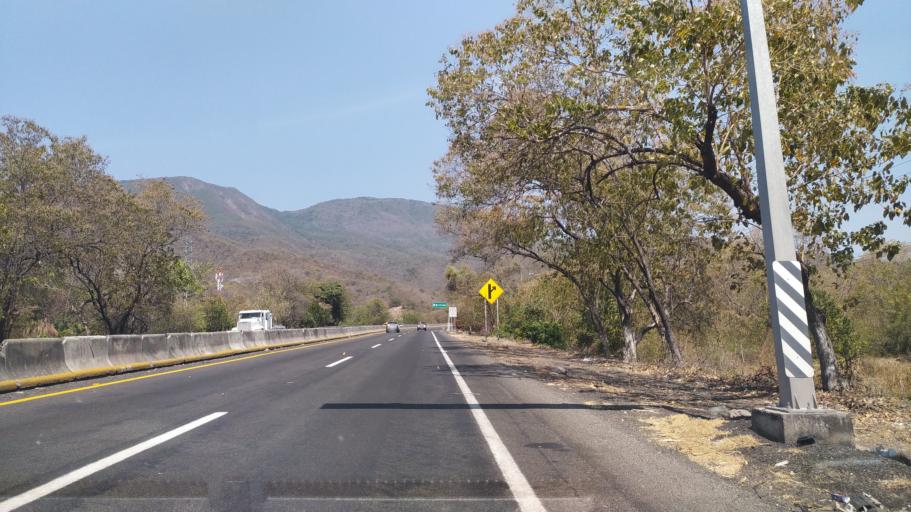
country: MX
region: Colima
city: Madrid
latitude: 19.0144
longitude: -103.8305
